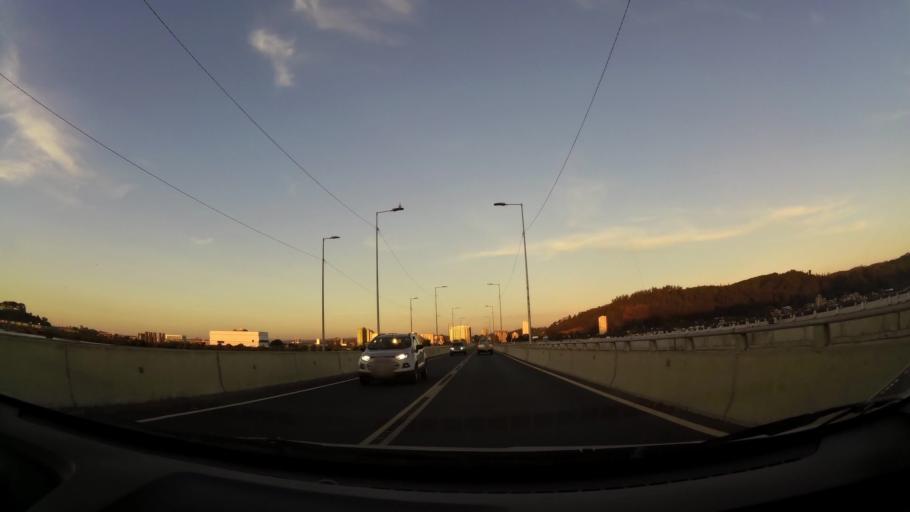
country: CL
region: Biobio
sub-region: Provincia de Concepcion
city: Concepcion
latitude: -36.8396
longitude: -73.0691
